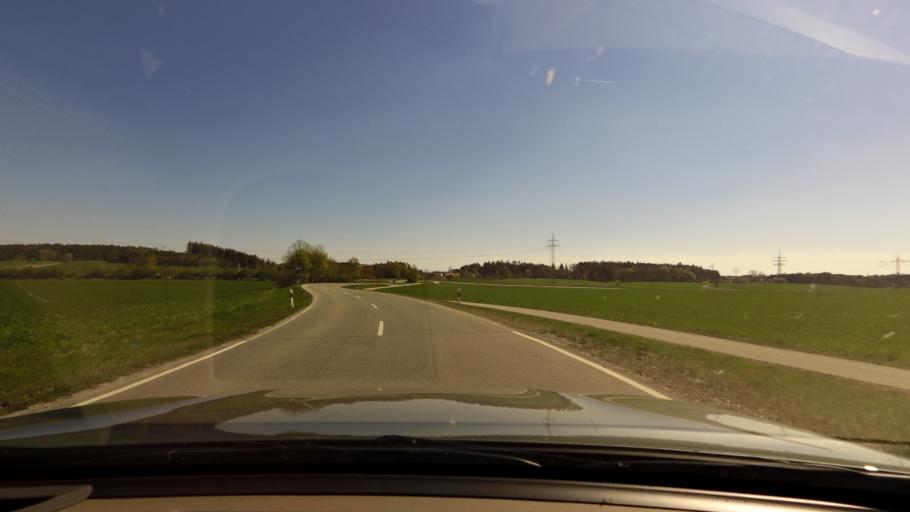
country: DE
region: Bavaria
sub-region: Upper Bavaria
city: Altdorf
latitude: 48.1520
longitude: 12.1827
